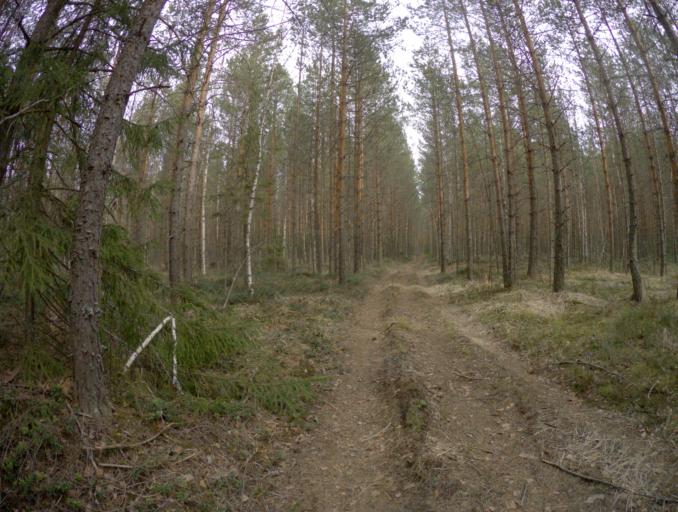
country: RU
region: Vladimir
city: Raduzhnyy
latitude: 55.9328
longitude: 40.2787
